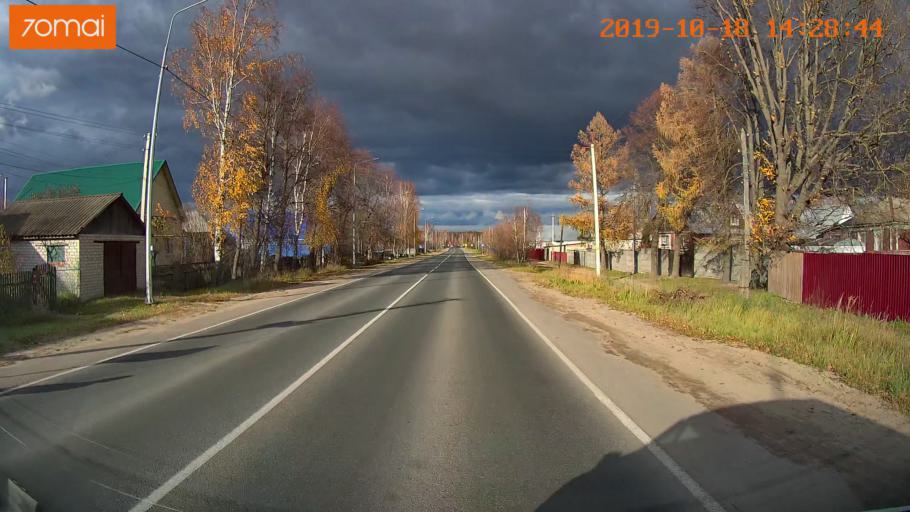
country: RU
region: Rjazan
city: Tuma
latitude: 55.1503
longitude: 40.5547
